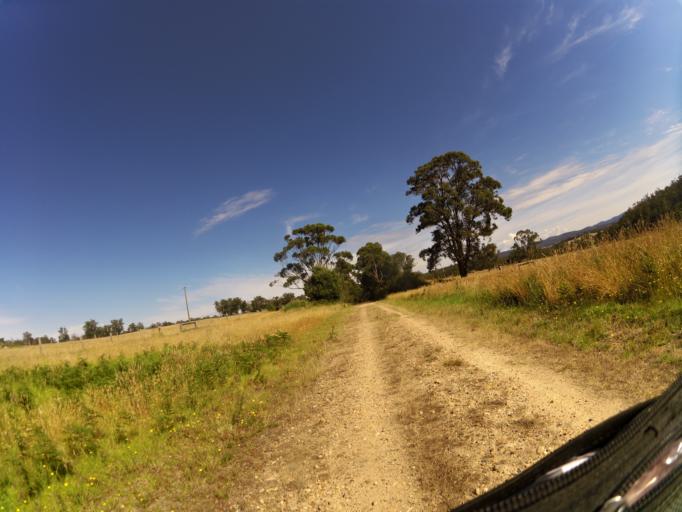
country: AU
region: Victoria
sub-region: East Gippsland
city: Lakes Entrance
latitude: -37.7381
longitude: 148.1680
